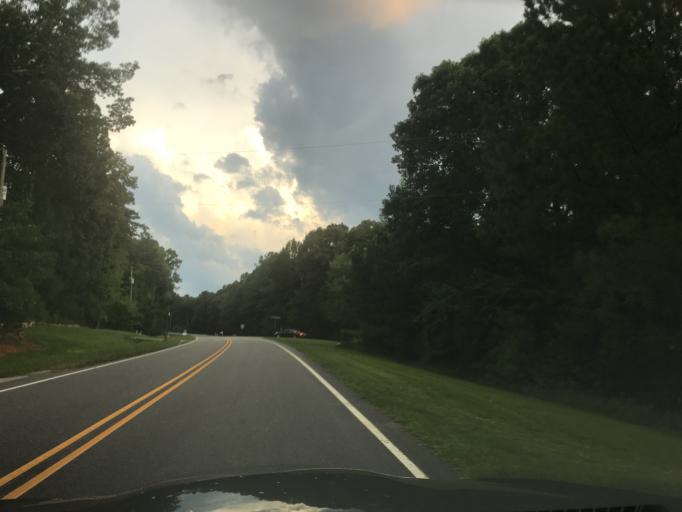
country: US
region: North Carolina
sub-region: Wake County
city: Wake Forest
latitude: 35.9481
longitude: -78.6104
